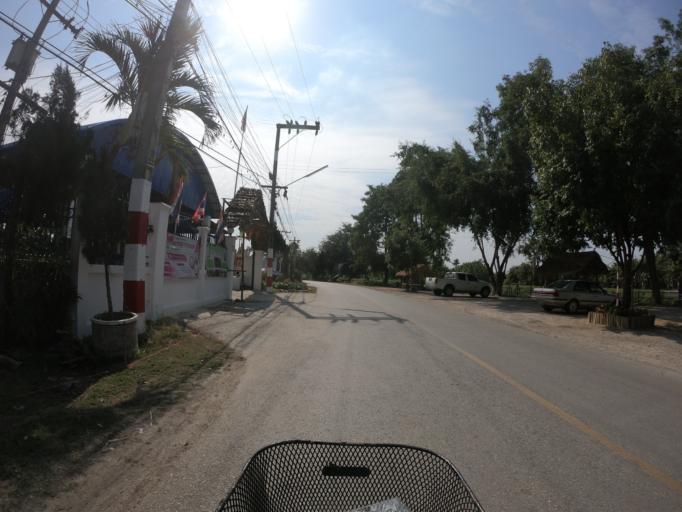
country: TH
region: Chiang Mai
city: Saraphi
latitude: 18.6991
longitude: 99.0580
